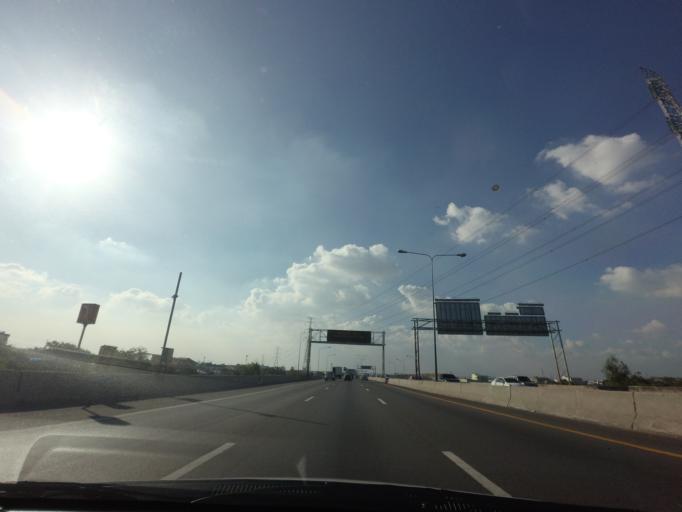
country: TH
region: Samut Prakan
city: Samut Prakan
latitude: 13.6225
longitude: 100.6041
